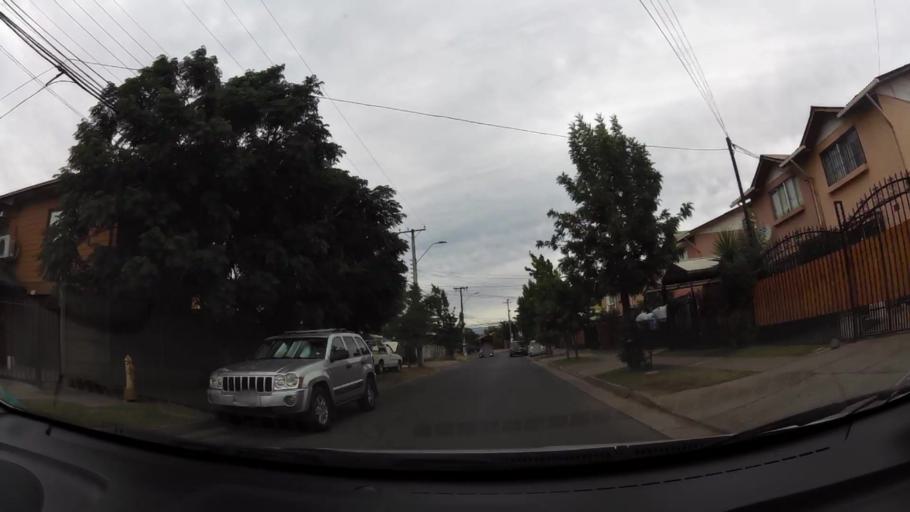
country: CL
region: O'Higgins
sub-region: Provincia de Cachapoal
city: Rancagua
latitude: -34.1299
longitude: -70.7368
